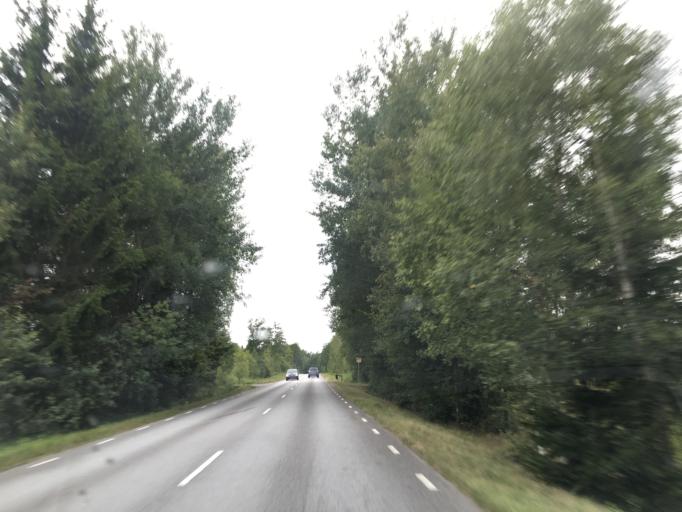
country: SE
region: Kalmar
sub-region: Nybro Kommun
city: Nybro
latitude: 56.7804
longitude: 15.9246
